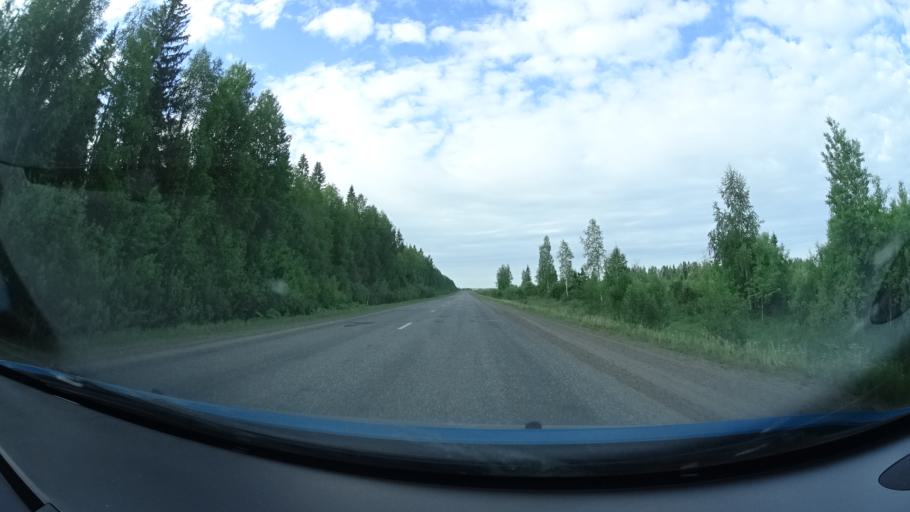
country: RU
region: Perm
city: Osa
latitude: 57.3861
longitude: 55.6087
